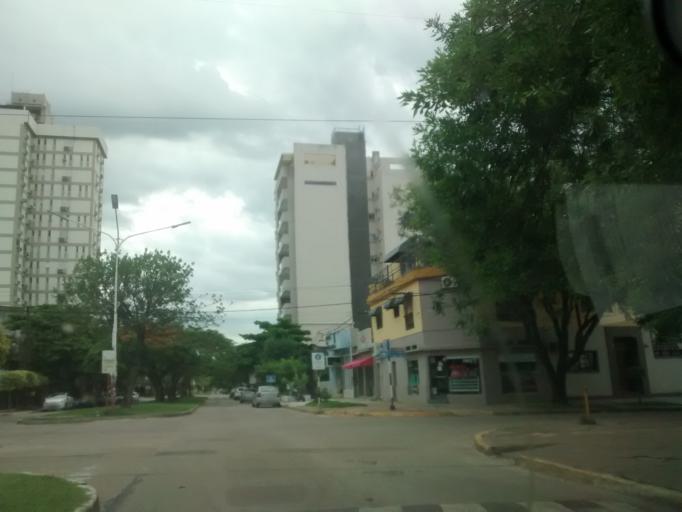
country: AR
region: Chaco
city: Resistencia
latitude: -27.4458
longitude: -58.9893
